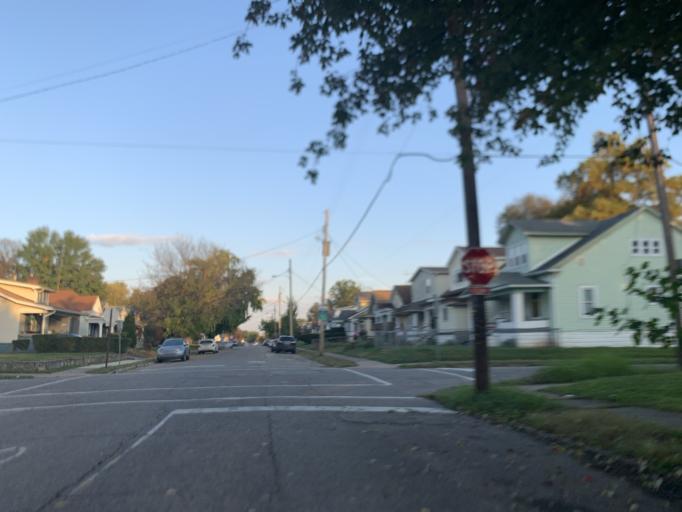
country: US
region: Indiana
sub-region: Floyd County
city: New Albany
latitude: 38.2572
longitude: -85.8225
